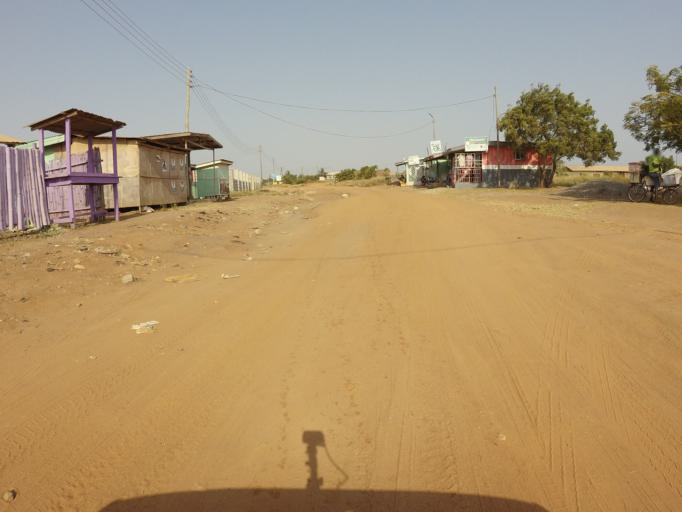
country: GH
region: Greater Accra
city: Tema
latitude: 5.7049
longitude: 0.0578
